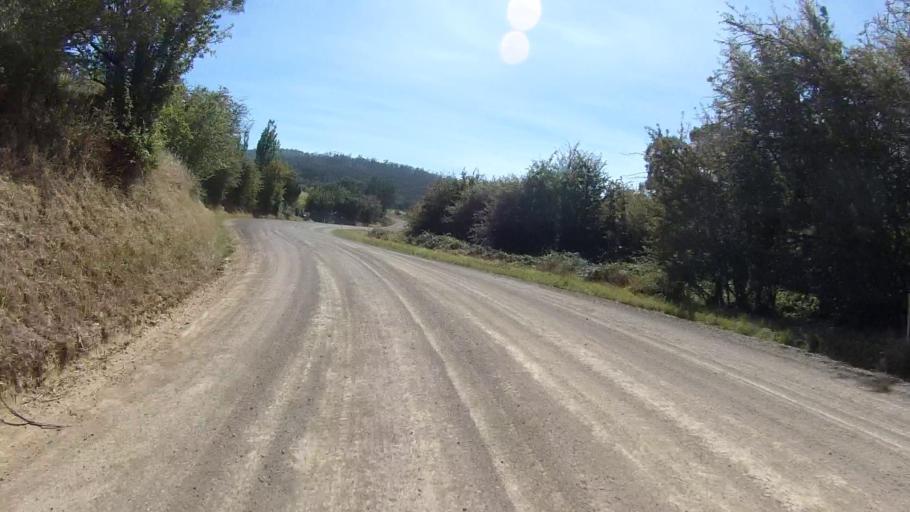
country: AU
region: Tasmania
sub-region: Sorell
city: Sorell
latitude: -42.7580
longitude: 147.6588
